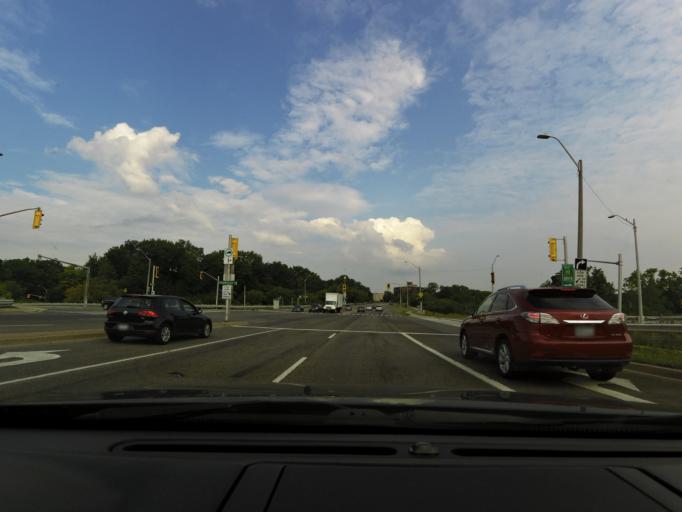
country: CA
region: Ontario
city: Hamilton
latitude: 43.2267
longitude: -79.7908
